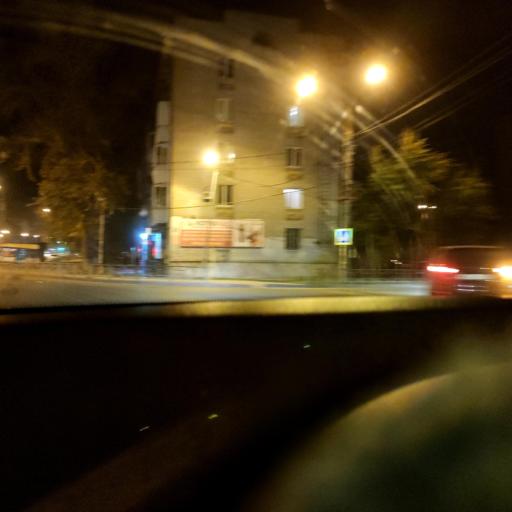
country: RU
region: Samara
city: Samara
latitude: 53.2037
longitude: 50.2395
